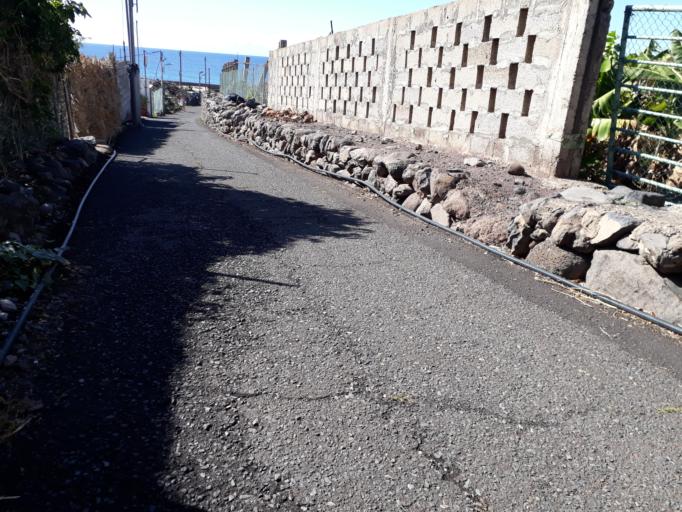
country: ES
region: Canary Islands
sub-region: Provincia de Santa Cruz de Tenerife
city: Alajero
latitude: 28.0918
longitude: -17.3374
